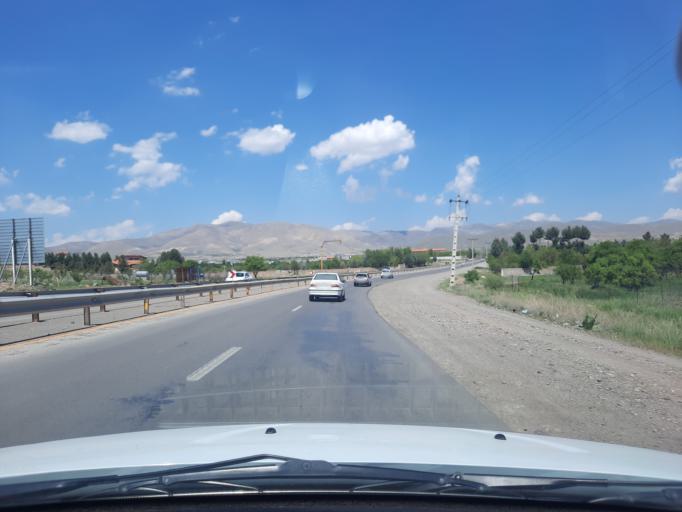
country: IR
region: Qazvin
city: Alvand
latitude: 36.2929
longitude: 50.1352
